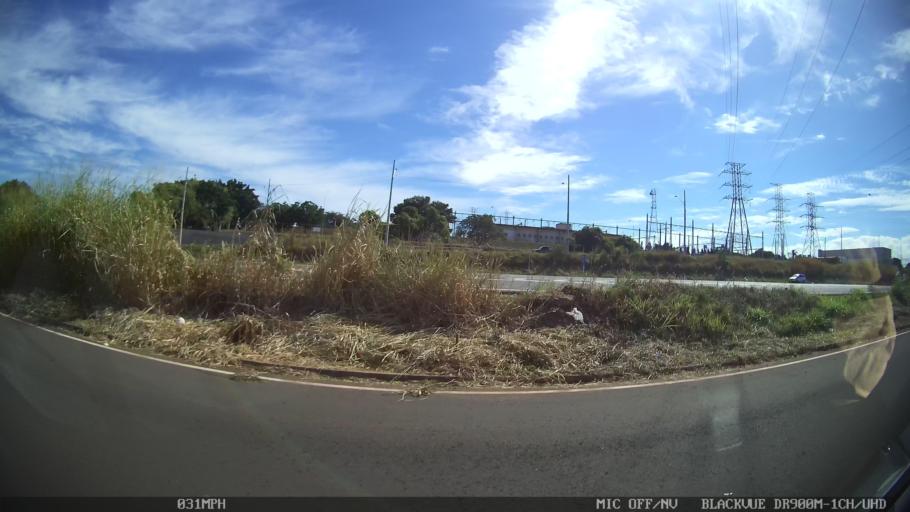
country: BR
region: Sao Paulo
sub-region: Sao Jose Do Rio Preto
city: Sao Jose do Rio Preto
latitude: -20.8441
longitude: -49.3719
